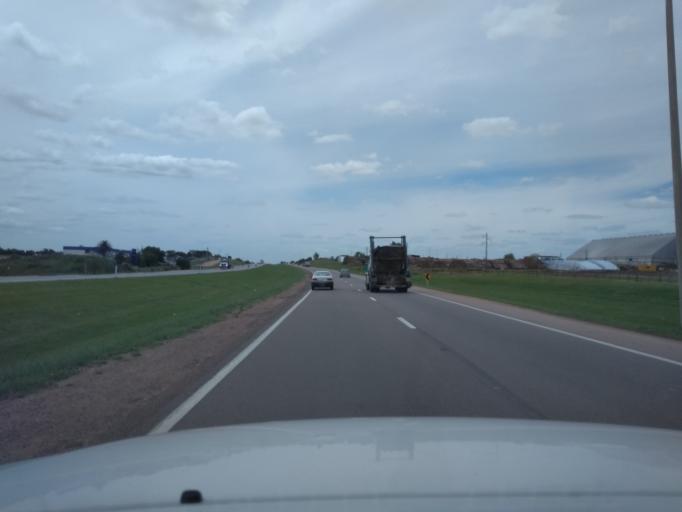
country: UY
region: Canelones
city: La Paz
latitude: -34.7470
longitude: -56.2533
